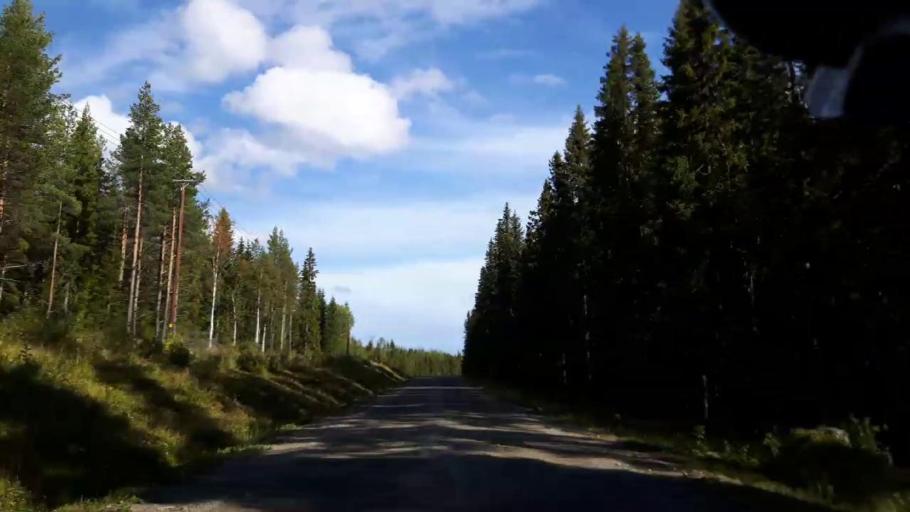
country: SE
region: Jaemtland
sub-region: Ragunda Kommun
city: Hammarstrand
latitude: 63.4341
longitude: 16.0340
